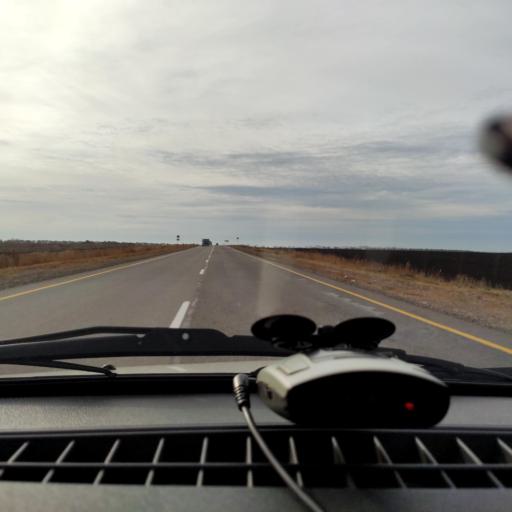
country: RU
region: Voronezj
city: Strelitsa
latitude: 51.4744
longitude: 38.9605
